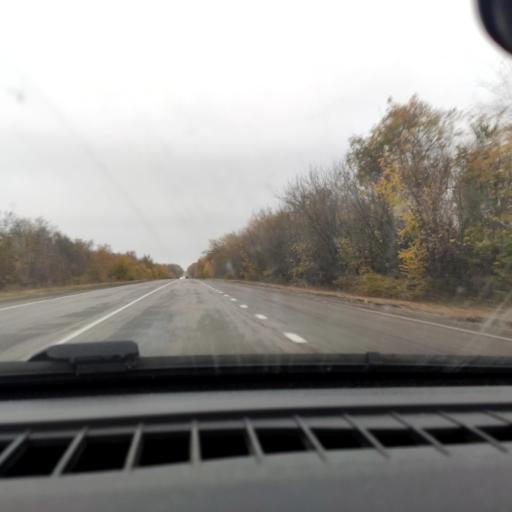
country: RU
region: Voronezj
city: Uryv-Pokrovka
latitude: 51.1501
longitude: 39.0613
